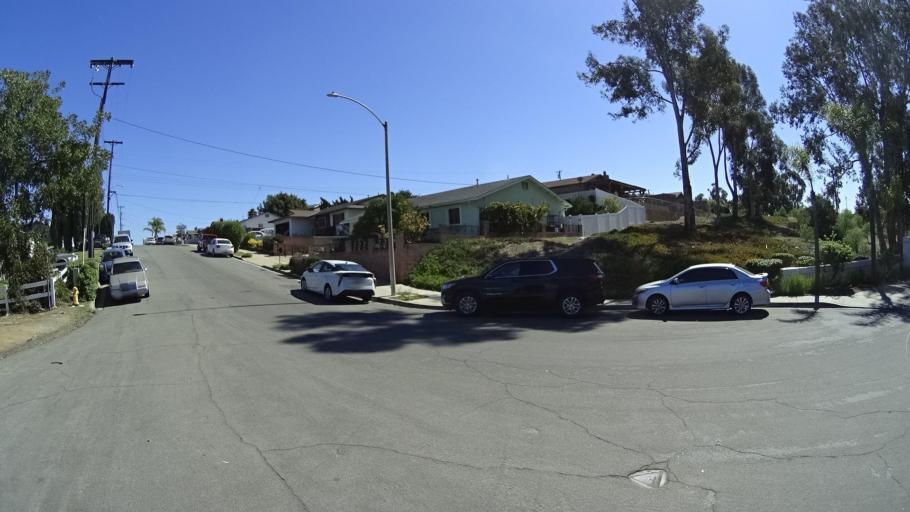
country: US
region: California
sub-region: San Diego County
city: La Presa
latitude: 32.6971
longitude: -117.0105
